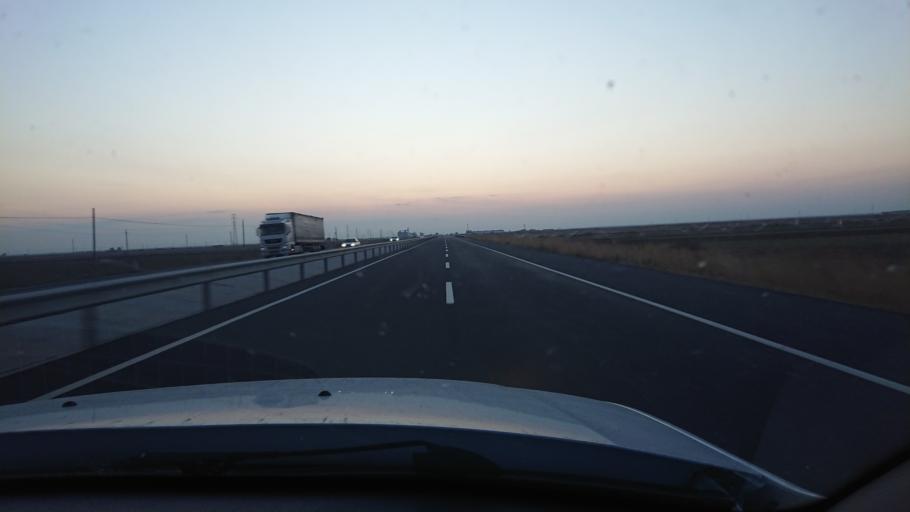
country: TR
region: Aksaray
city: Yesilova
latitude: 38.3128
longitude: 33.8391
